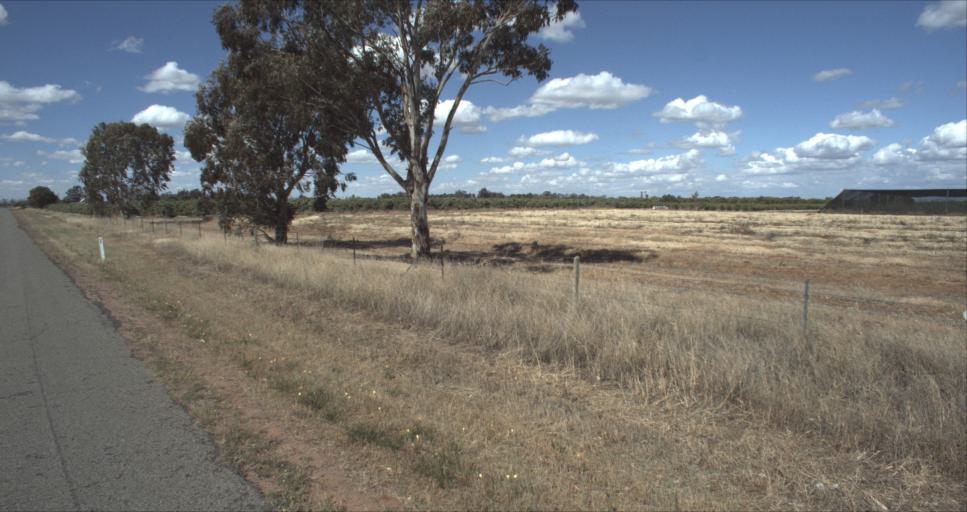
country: AU
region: New South Wales
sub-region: Leeton
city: Leeton
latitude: -34.5155
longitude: 146.2380
